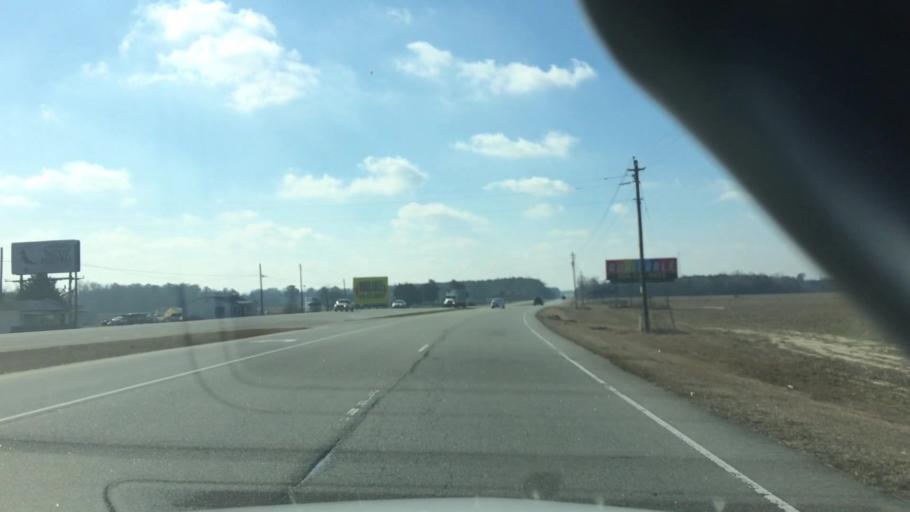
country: US
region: North Carolina
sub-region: Pitt County
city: Grifton
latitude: 35.3494
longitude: -77.4682
